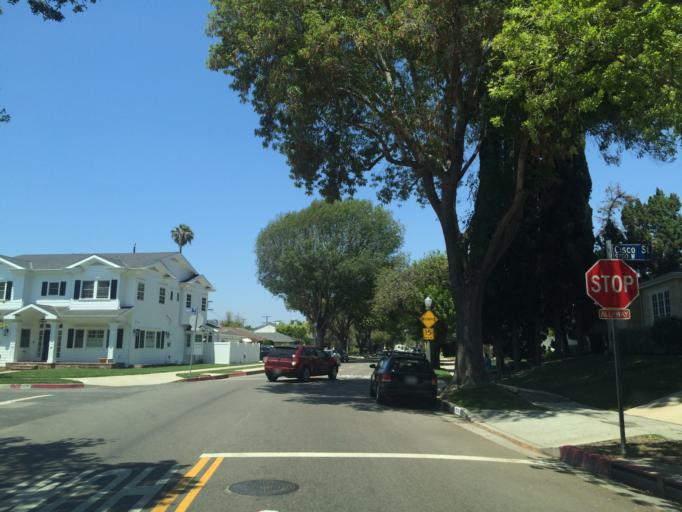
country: US
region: California
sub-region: Los Angeles County
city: Culver City
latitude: 34.0436
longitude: -118.3977
